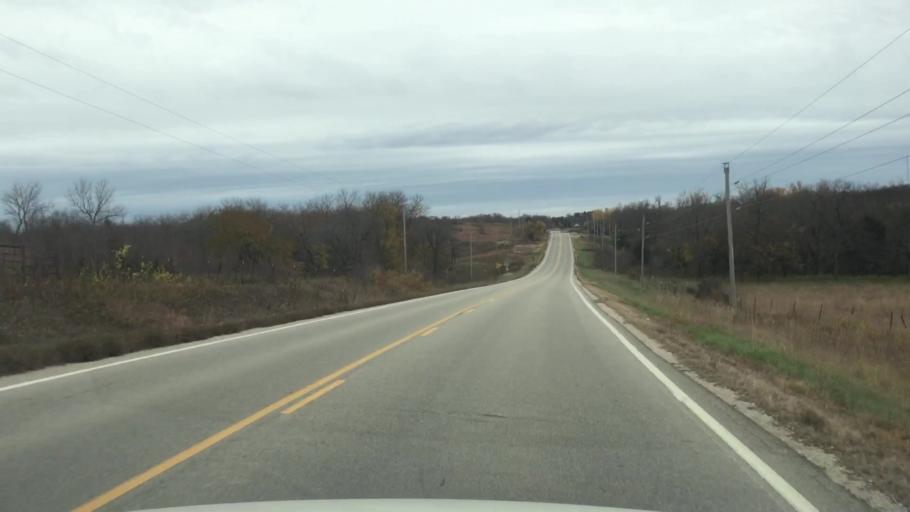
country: US
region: Kansas
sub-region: Pottawatomie County
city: Wamego
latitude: 39.1248
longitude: -96.2943
